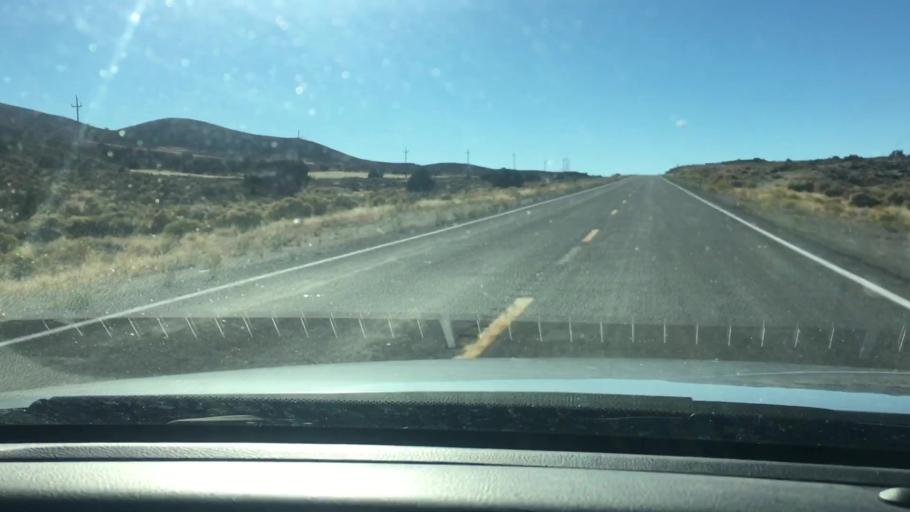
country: US
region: Nevada
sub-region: Nye County
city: Tonopah
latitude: 38.1717
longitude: -116.4200
